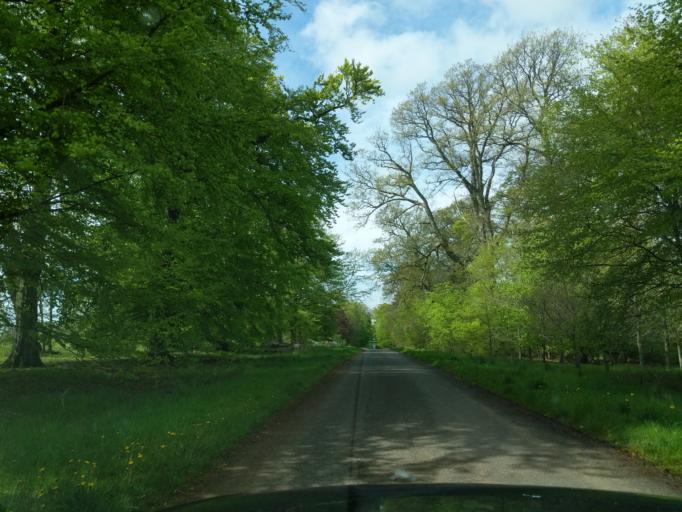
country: GB
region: Scotland
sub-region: The Scottish Borders
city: Saint Boswells
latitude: 55.6489
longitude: -2.5574
